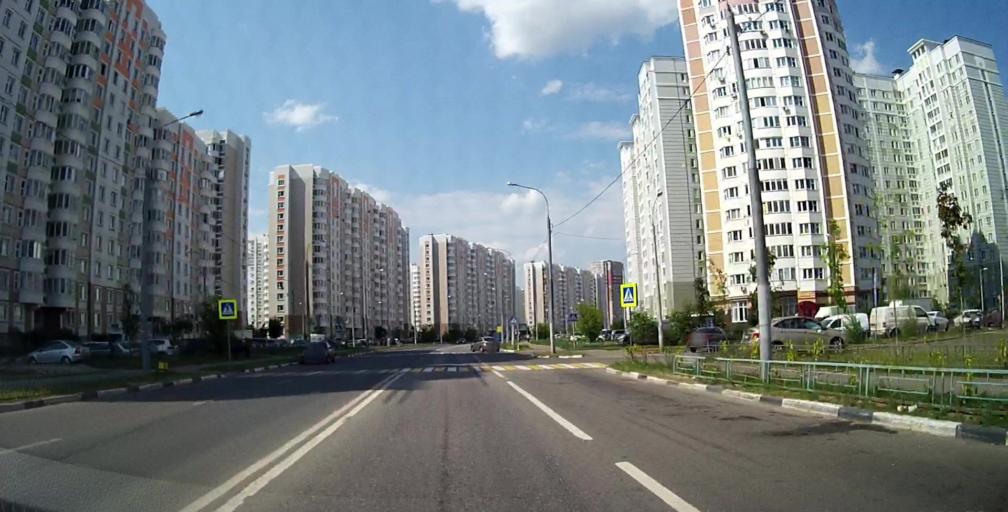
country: RU
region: Moskovskaya
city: Dubrovitsy
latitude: 55.4134
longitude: 37.4816
